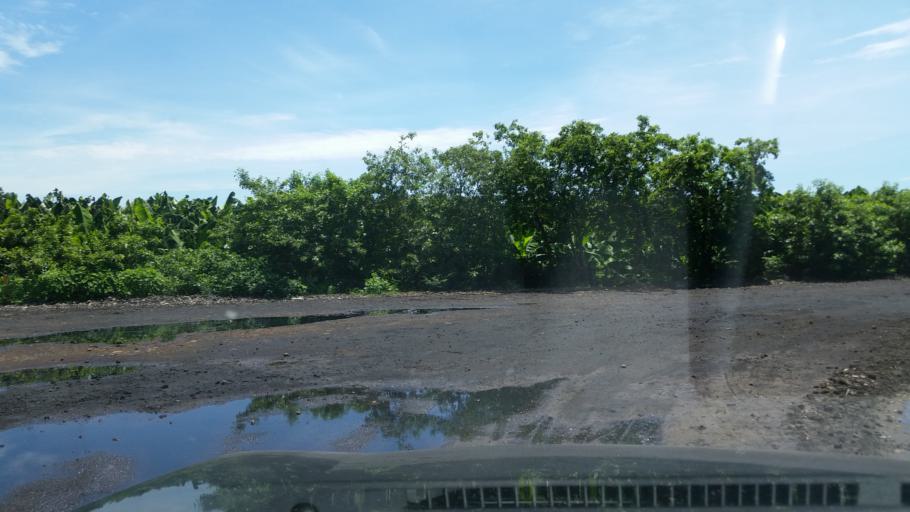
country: NI
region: Chinandega
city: Puerto Morazan
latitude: 12.7647
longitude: -87.1214
